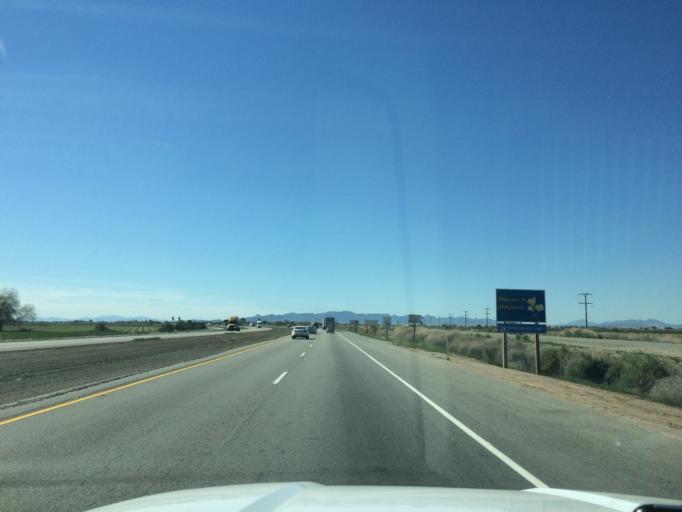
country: US
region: Arizona
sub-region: La Paz County
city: Ehrenberg
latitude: 33.6070
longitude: -114.5399
